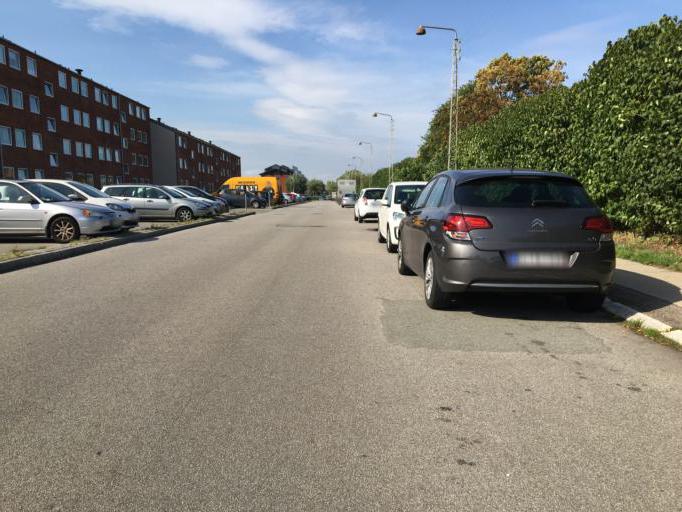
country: DK
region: Capital Region
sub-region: Tarnby Kommune
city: Tarnby
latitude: 55.6323
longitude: 12.6112
